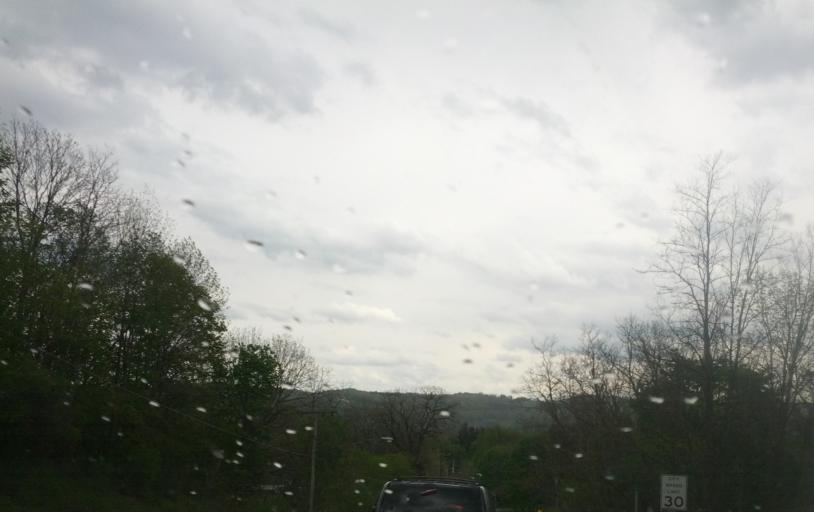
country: US
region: New York
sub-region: Onondaga County
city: Nedrow
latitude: 43.0042
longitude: -76.1612
